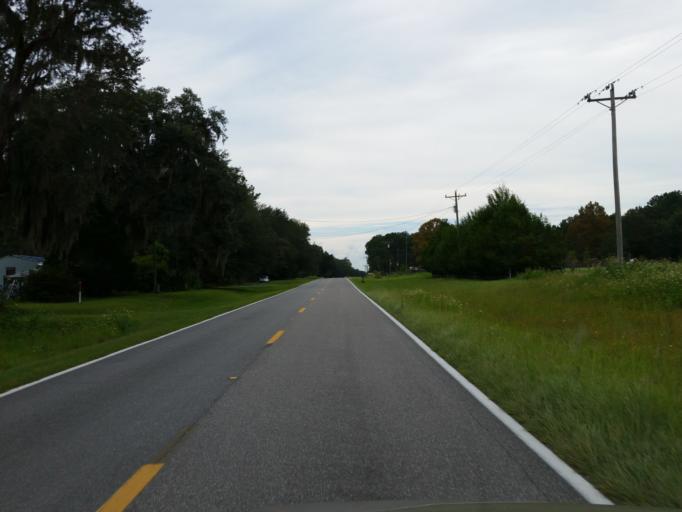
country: US
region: Florida
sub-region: Alachua County
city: High Springs
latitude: 29.9498
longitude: -82.5577
